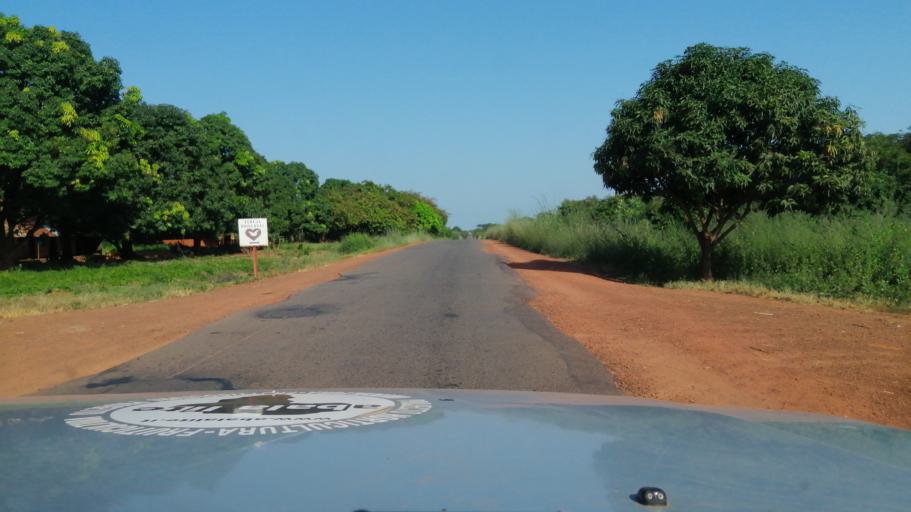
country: GW
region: Bissau
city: Bissau
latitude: 11.9588
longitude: -15.5224
